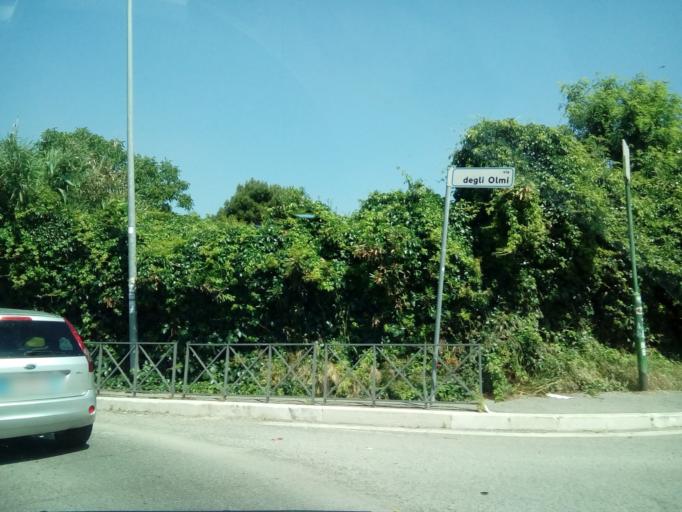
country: IT
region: Latium
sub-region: Citta metropolitana di Roma Capitale
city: Rome
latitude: 41.8793
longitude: 12.5819
